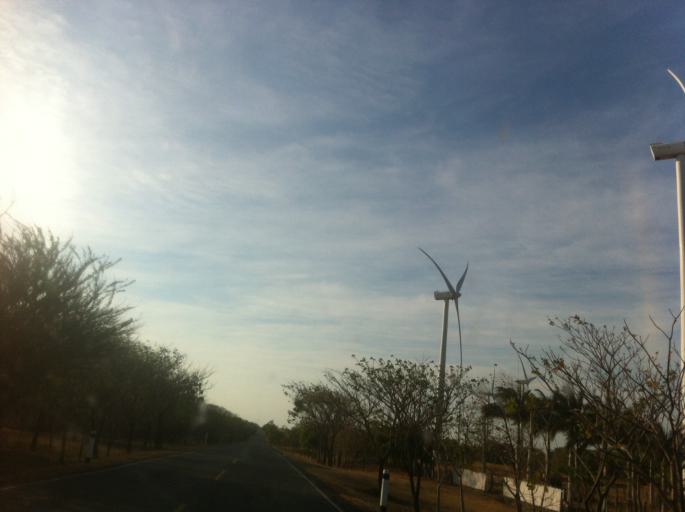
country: NI
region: Rivas
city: Rivas
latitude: 11.3357
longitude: -85.7271
